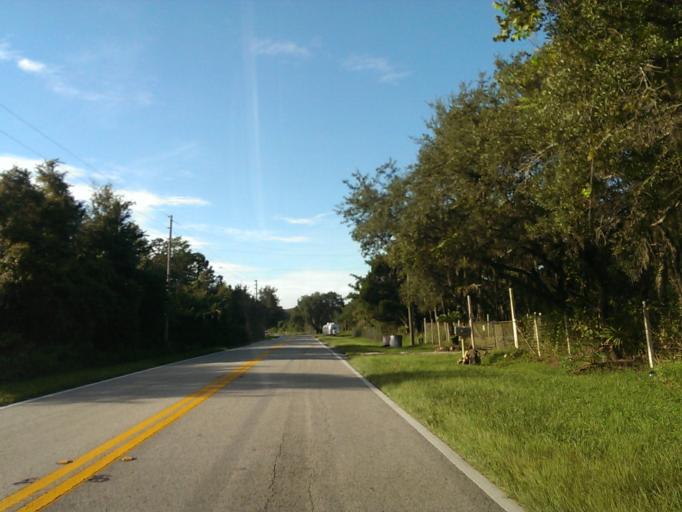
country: US
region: Florida
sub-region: Polk County
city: Citrus Ridge
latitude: 28.3656
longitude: -81.6460
